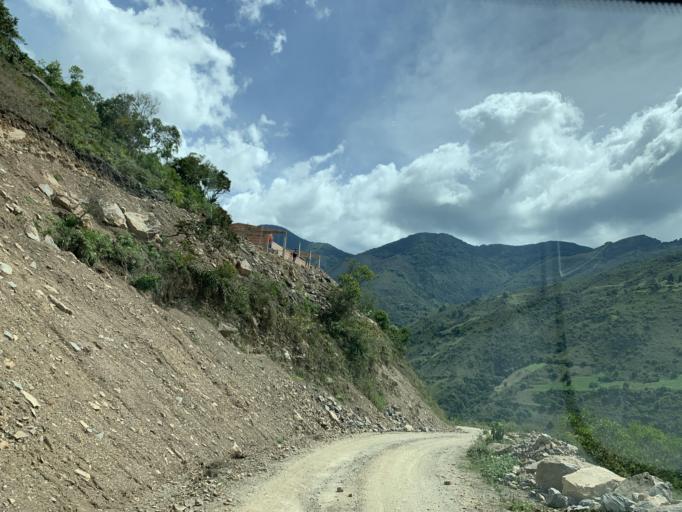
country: CO
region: Boyaca
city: Tipacoque
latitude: 6.4512
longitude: -72.7073
